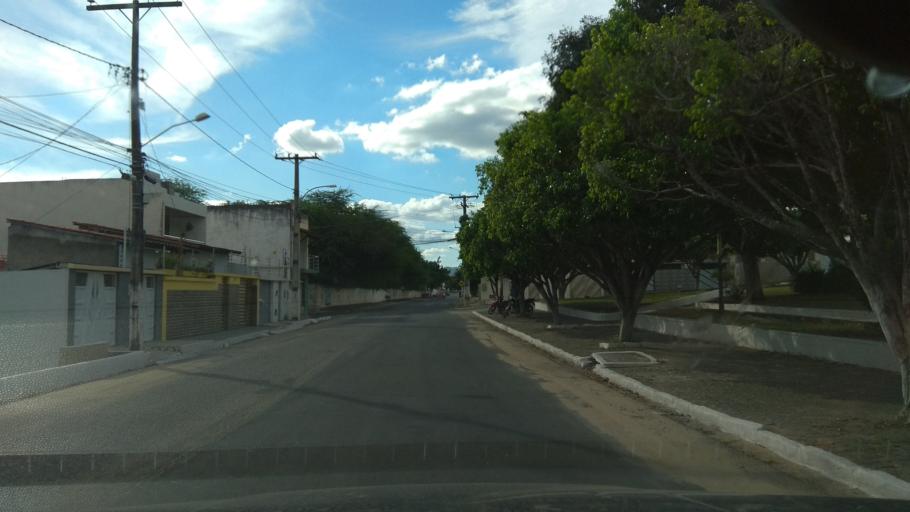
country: BR
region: Bahia
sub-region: Jequie
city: Jequie
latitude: -13.8727
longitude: -40.0752
